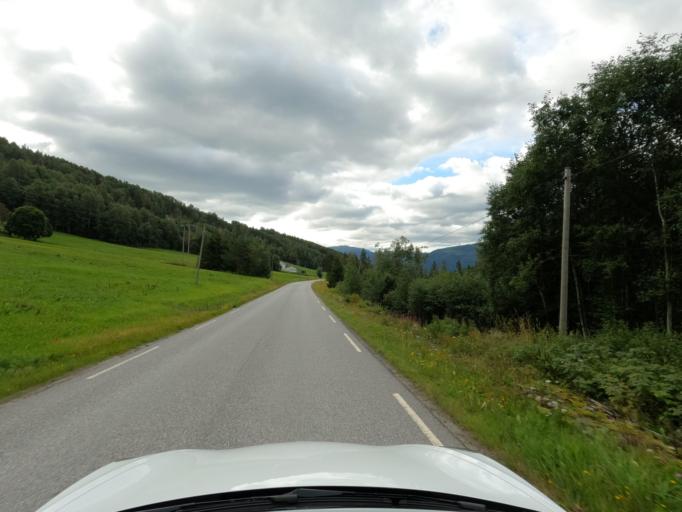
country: NO
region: Buskerud
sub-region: Nore og Uvdal
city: Rodberg
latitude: 60.0155
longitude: 8.8374
